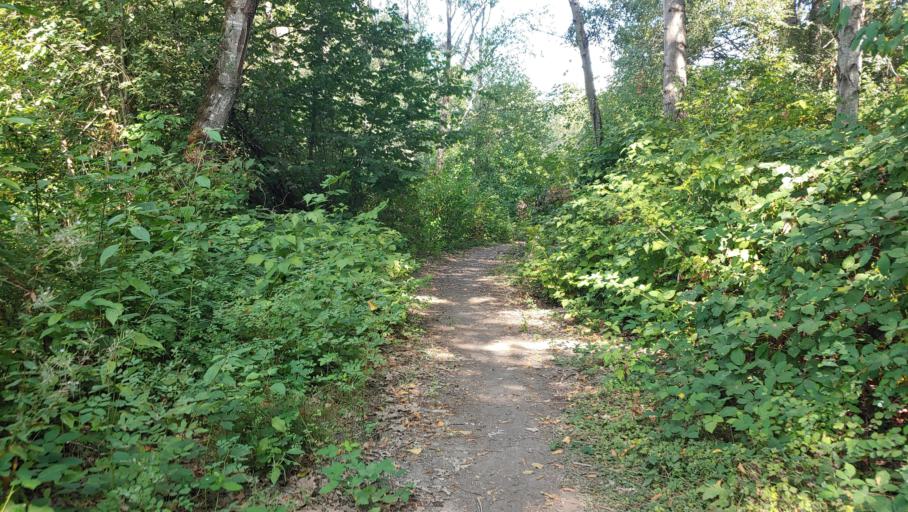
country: US
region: Washington
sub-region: King County
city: Bryn Mawr-Skyway
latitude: 47.4753
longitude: -122.2405
